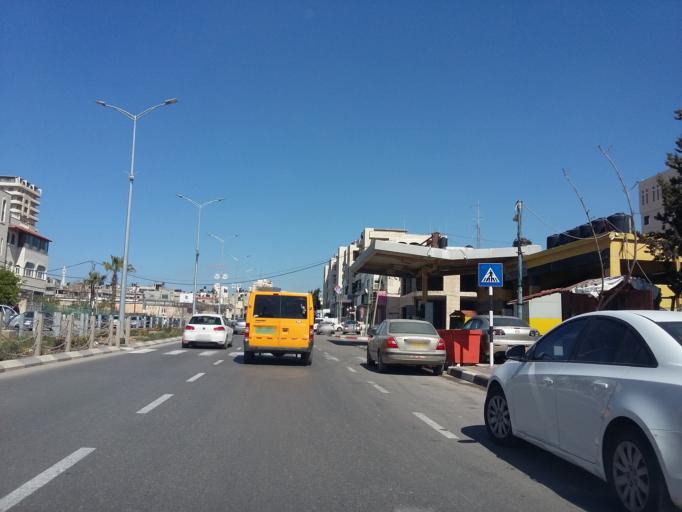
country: PS
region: West Bank
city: Ramallah
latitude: 31.8916
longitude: 35.2145
